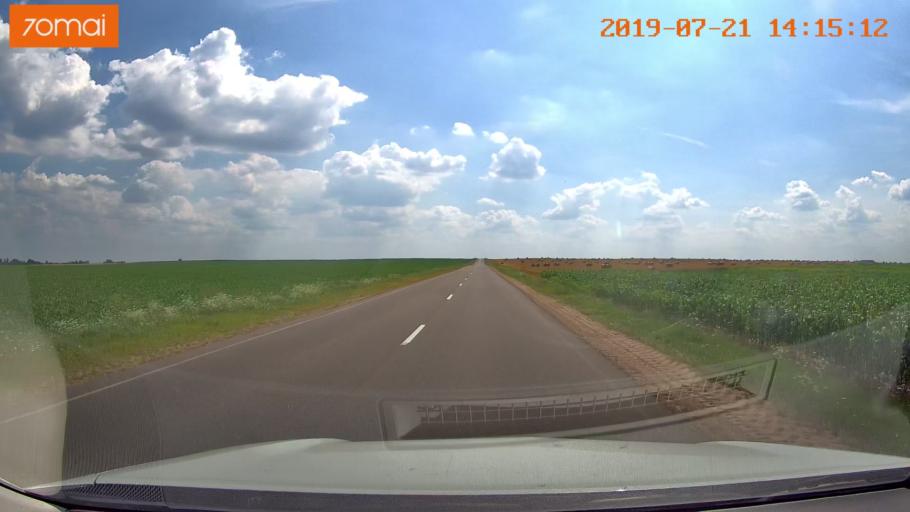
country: BY
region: Grodnenskaya
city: Karelichy
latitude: 53.6377
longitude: 26.1691
